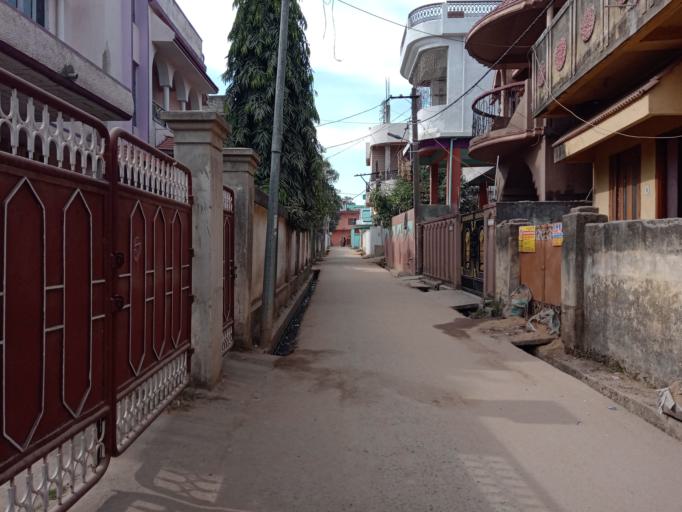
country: IN
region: Jharkhand
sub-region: Ranchi
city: Kanke
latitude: 23.3971
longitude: 85.3530
